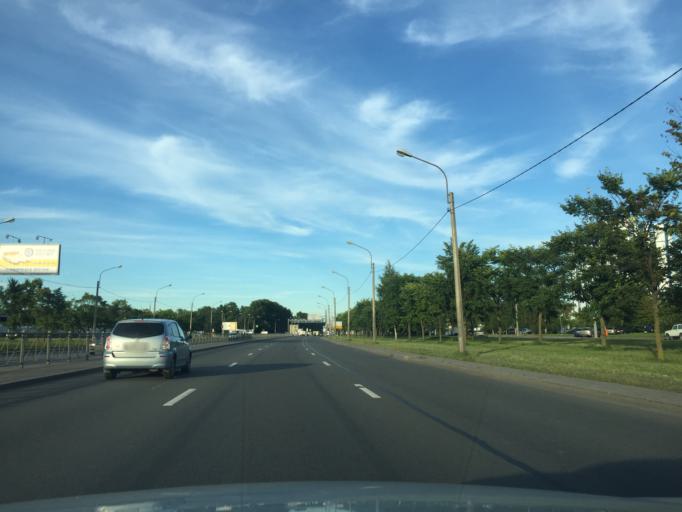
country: RU
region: St.-Petersburg
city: Obukhovo
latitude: 59.8456
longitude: 30.4248
